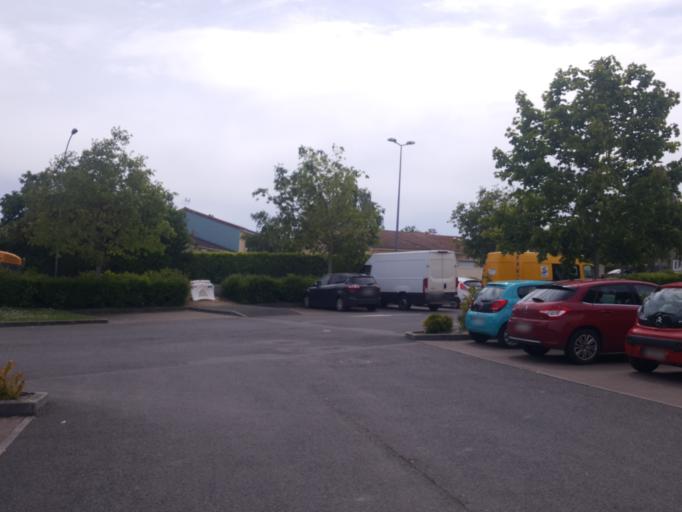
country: FR
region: Poitou-Charentes
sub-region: Departement de la Vienne
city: Chasseneuil-du-Poitou
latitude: 46.6124
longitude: 0.3665
